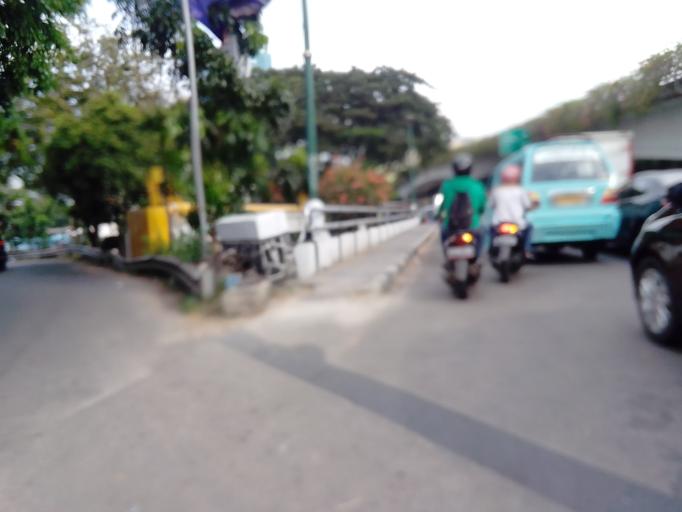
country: ID
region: Jakarta Raya
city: Jakarta
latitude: -6.1813
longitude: 106.8136
